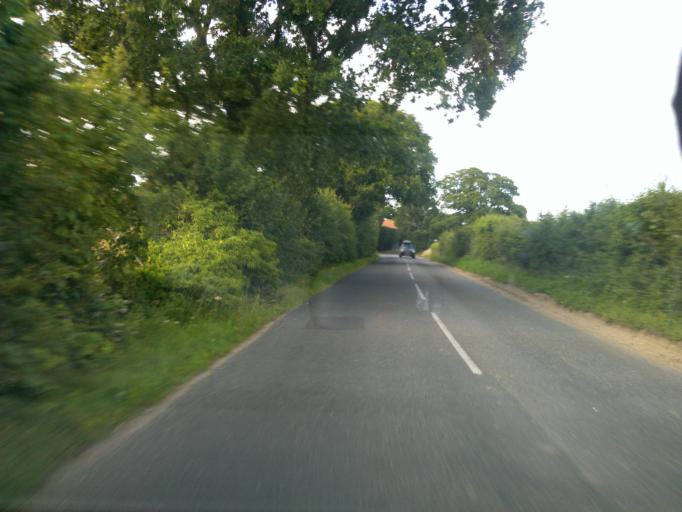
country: GB
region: England
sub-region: Essex
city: Great Bentley
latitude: 51.8620
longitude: 1.0664
